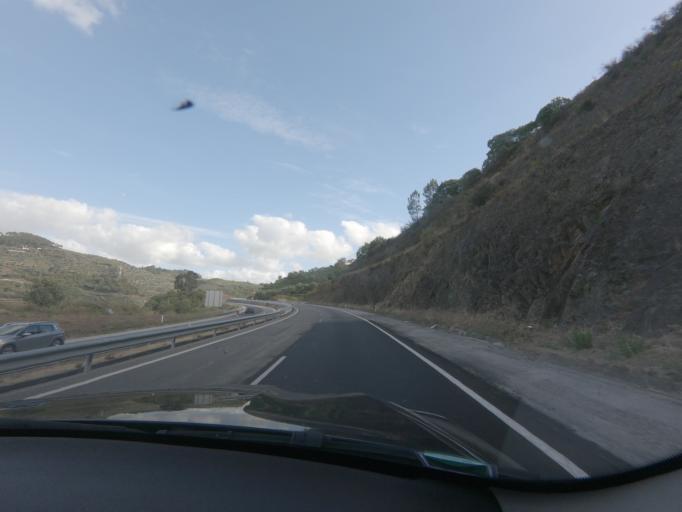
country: PT
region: Viseu
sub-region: Lamego
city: Lamego
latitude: 41.1069
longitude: -7.7766
